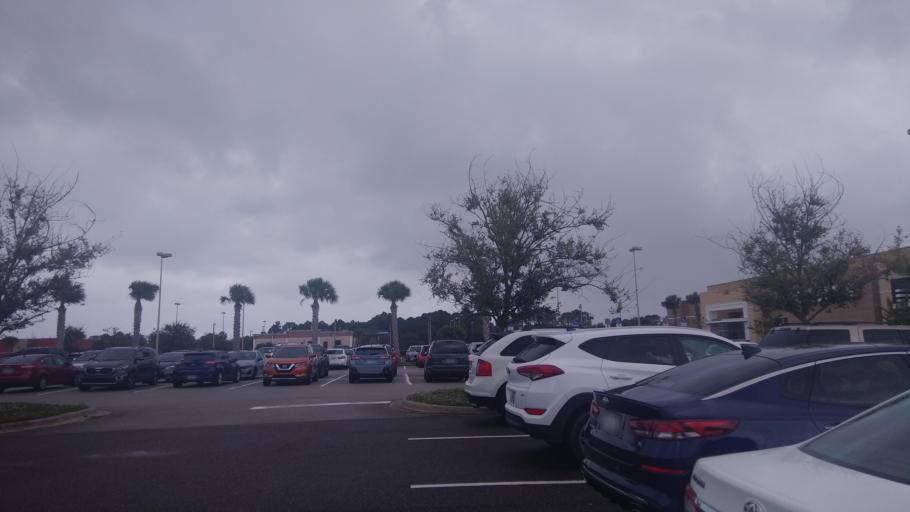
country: US
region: Florida
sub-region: Brevard County
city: West Melbourne
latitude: 28.0377
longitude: -80.6656
